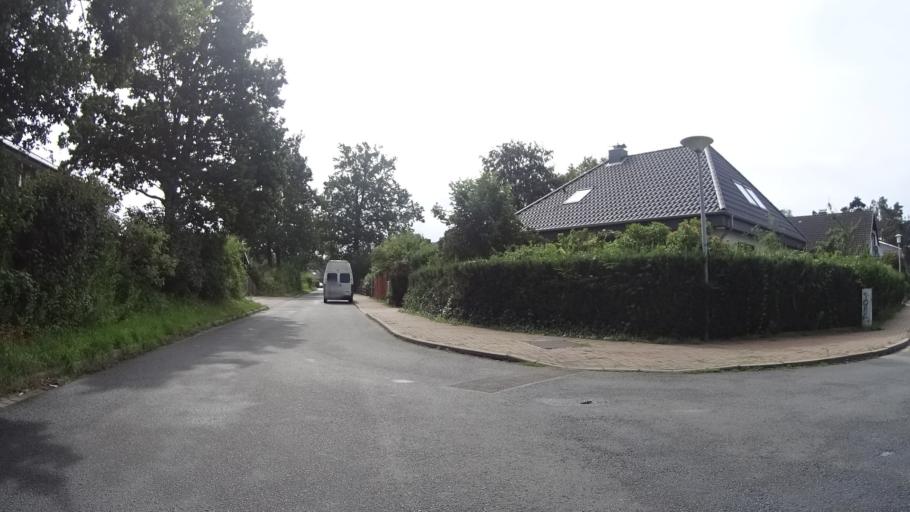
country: DE
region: Schleswig-Holstein
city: Henstedt-Ulzburg
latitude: 53.7629
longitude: 9.9912
